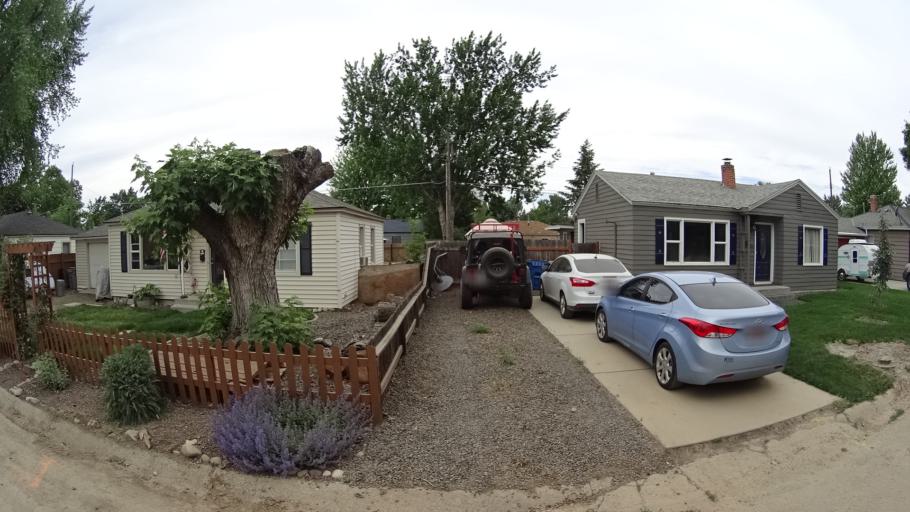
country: US
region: Idaho
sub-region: Ada County
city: Boise
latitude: 43.5807
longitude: -116.2177
